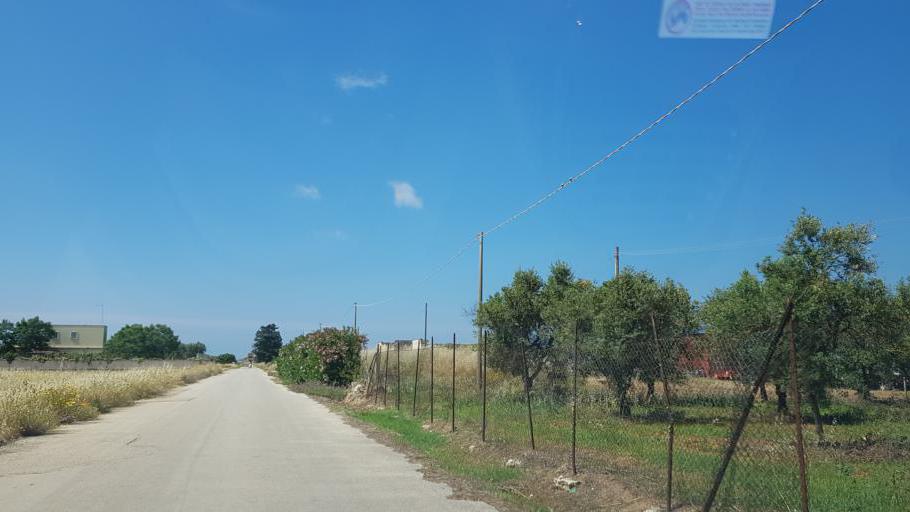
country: IT
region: Apulia
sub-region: Provincia di Brindisi
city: Brindisi
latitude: 40.6556
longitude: 17.8527
